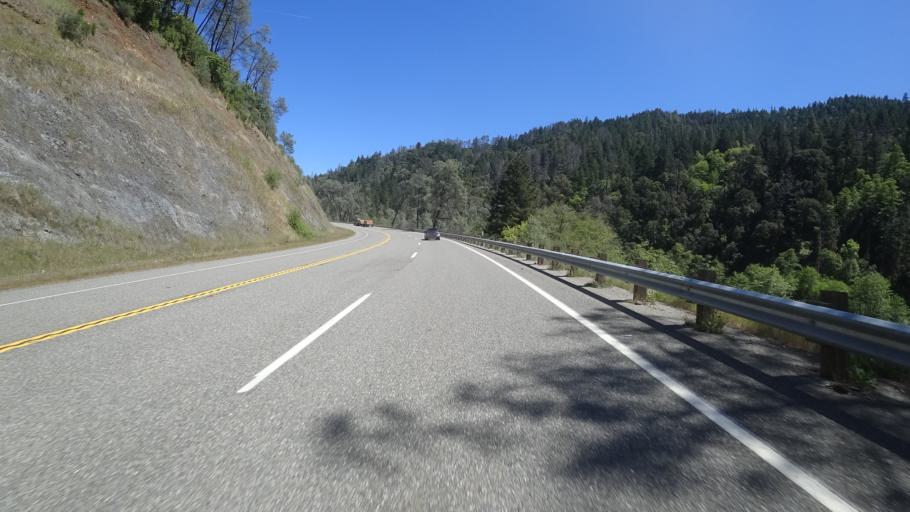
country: US
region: California
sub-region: Trinity County
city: Hayfork
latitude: 40.7354
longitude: -123.2314
